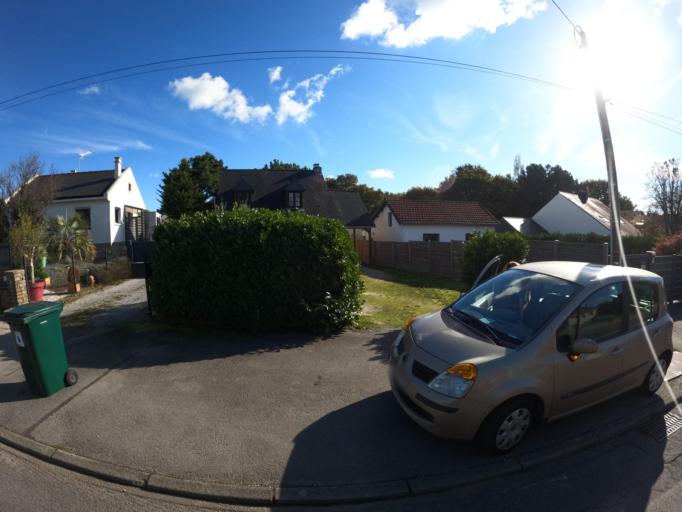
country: FR
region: Pays de la Loire
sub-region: Departement de la Loire-Atlantique
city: La Baule-Escoublac
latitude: 47.2936
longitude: -2.3630
